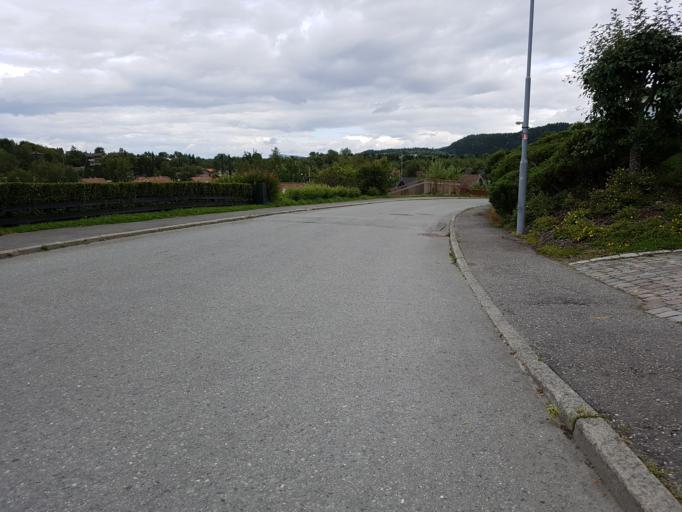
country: NO
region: Sor-Trondelag
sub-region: Trondheim
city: Trondheim
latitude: 63.4005
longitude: 10.4492
